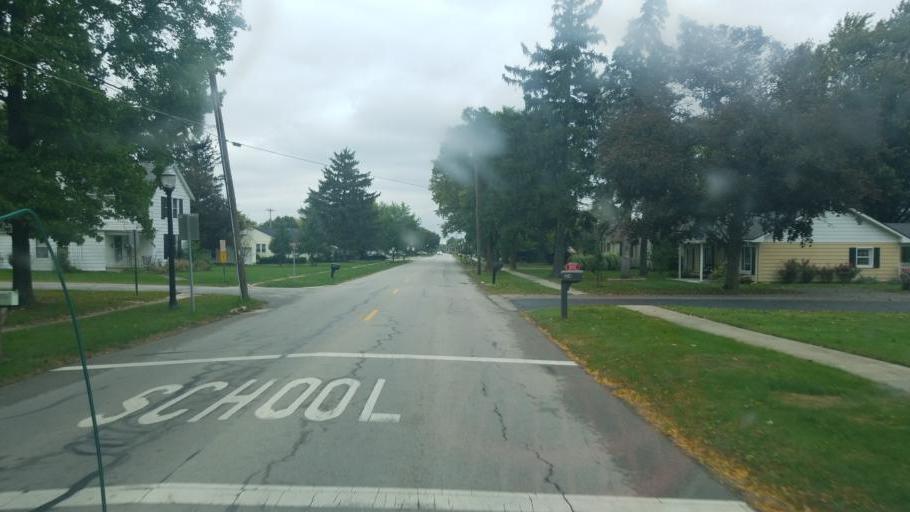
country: US
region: Ohio
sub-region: Wood County
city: Haskins
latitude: 41.4670
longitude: -83.7059
